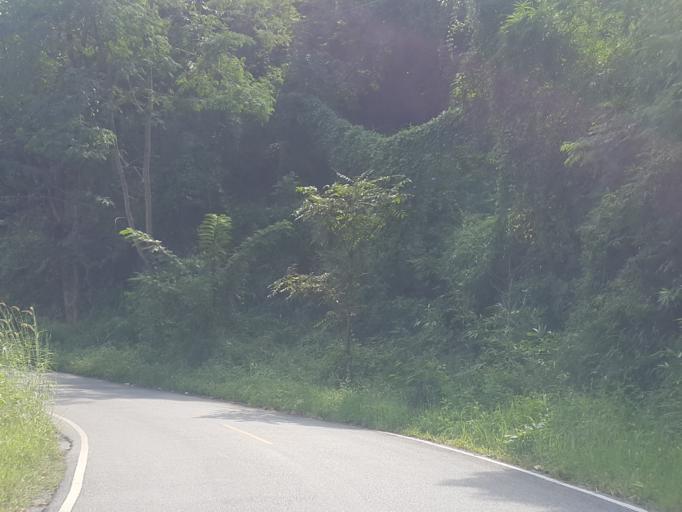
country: TH
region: Chiang Mai
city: Mae On
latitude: 18.8639
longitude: 99.2853
